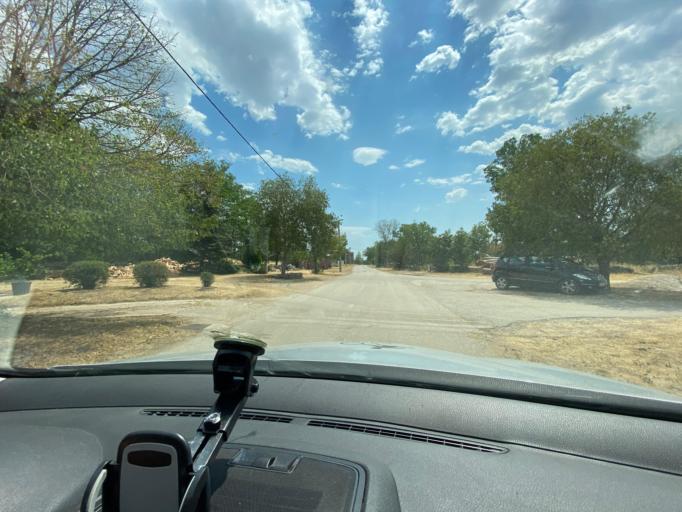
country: HR
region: Splitsko-Dalmatinska
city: Hrvace
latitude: 43.7934
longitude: 16.6195
